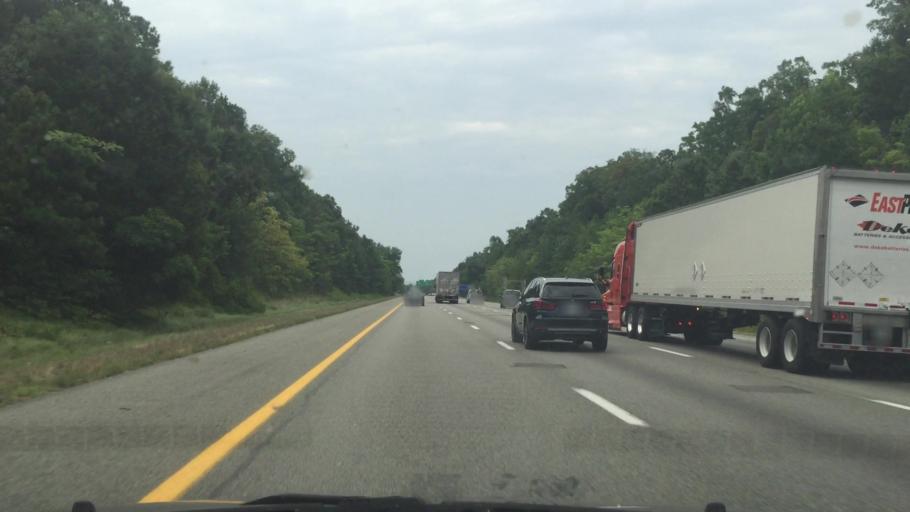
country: US
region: Virginia
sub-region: Hanover County
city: Mechanicsville
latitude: 37.5903
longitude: -77.3430
